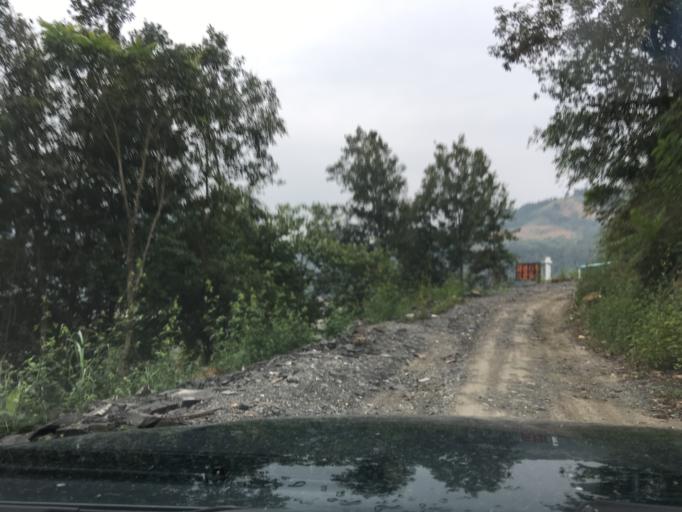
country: CN
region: Guangxi Zhuangzu Zizhiqu
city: Xinzhou
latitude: 25.0500
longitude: 105.9183
